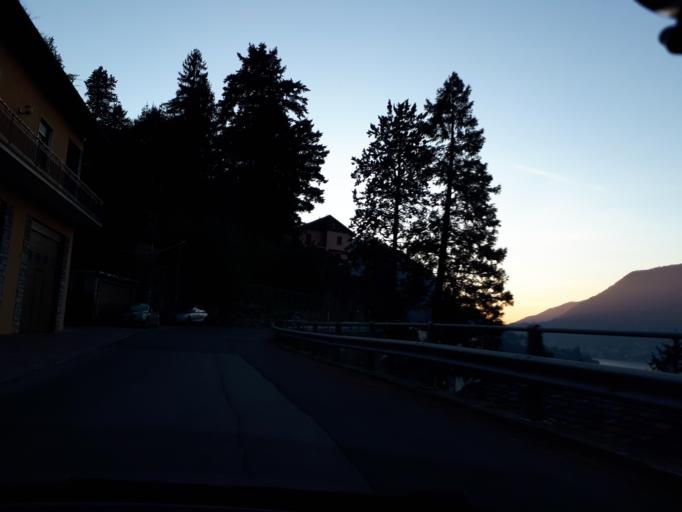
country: IT
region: Lombardy
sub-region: Provincia di Como
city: Faggeto Lario
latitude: 45.8623
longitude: 9.1489
